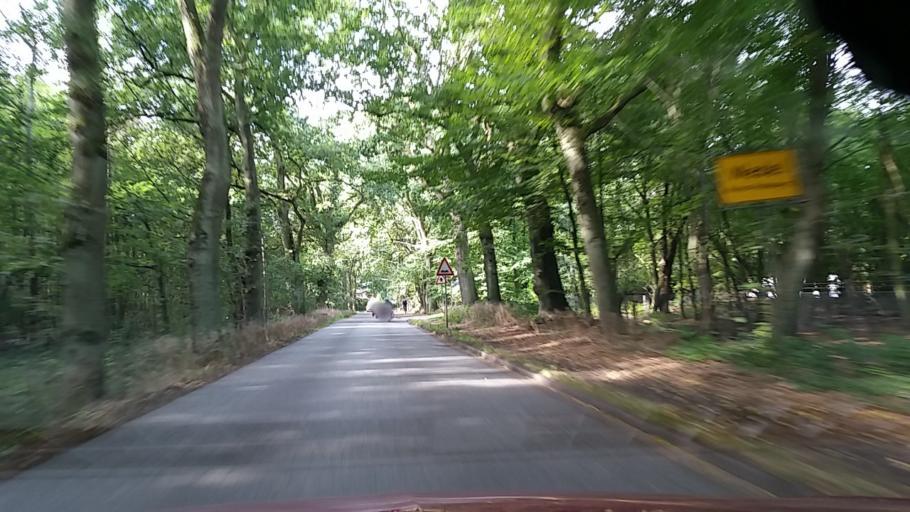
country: DE
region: Schleswig-Holstein
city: Wedel
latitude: 53.5980
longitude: 9.7342
